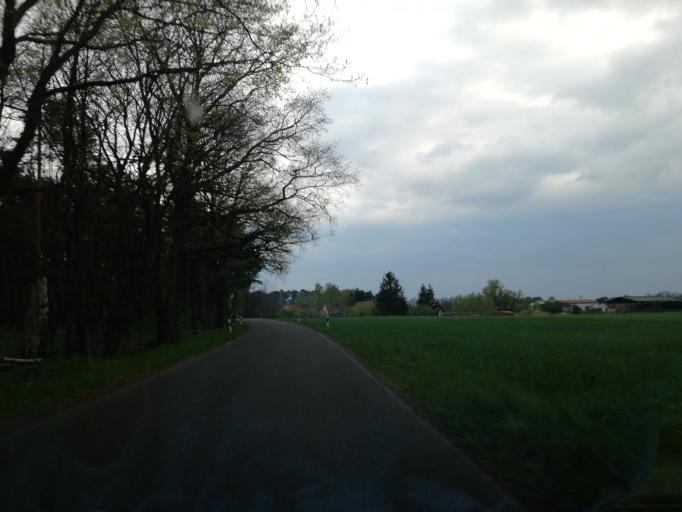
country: DE
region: Brandenburg
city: Calau
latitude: 51.7898
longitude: 13.8866
